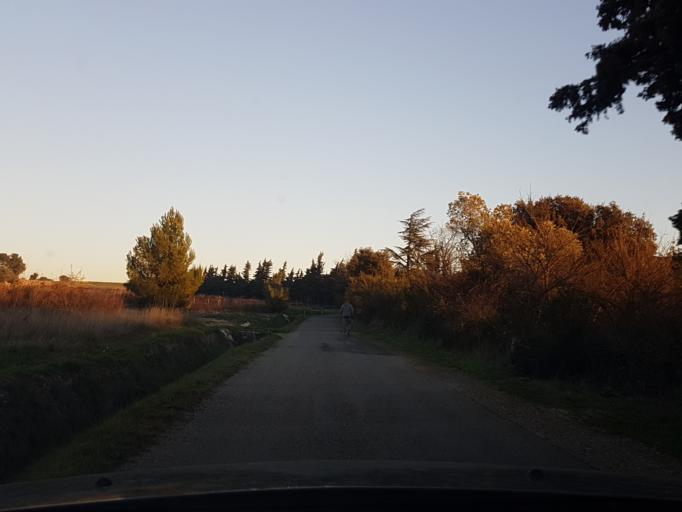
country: FR
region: Provence-Alpes-Cote d'Azur
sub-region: Departement du Vaucluse
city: Vedene
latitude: 43.9639
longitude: 4.9079
